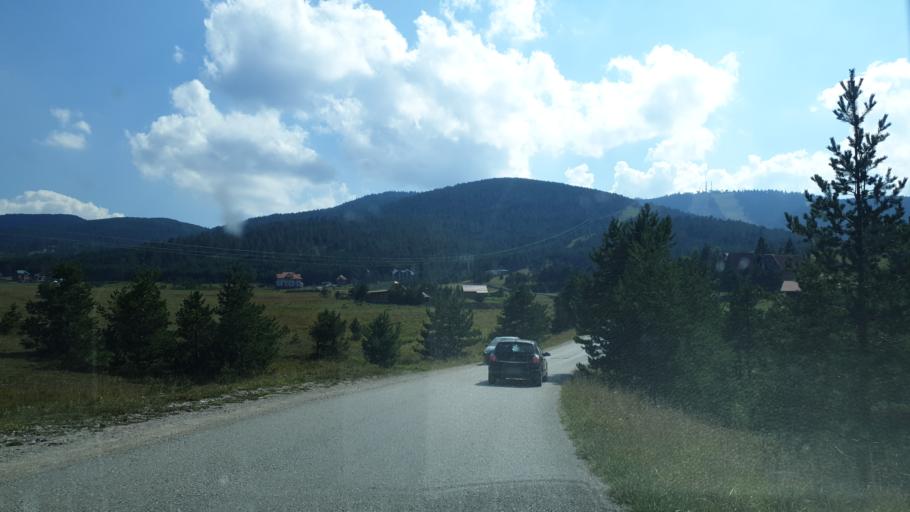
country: RS
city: Zlatibor
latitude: 43.6767
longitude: 19.6555
